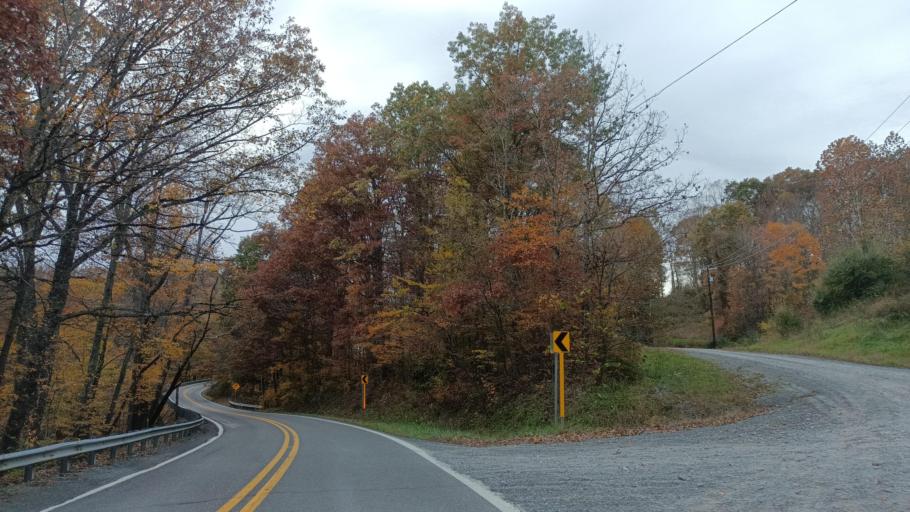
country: US
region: West Virginia
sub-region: Taylor County
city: Grafton
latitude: 39.3338
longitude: -79.8864
